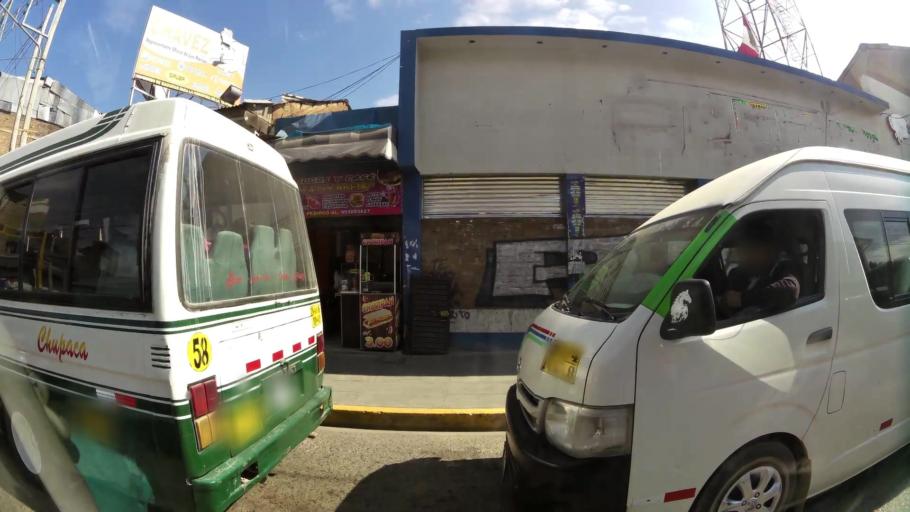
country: PE
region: Junin
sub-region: Provincia de Huancayo
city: Huancayo
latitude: -12.0672
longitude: -75.2076
